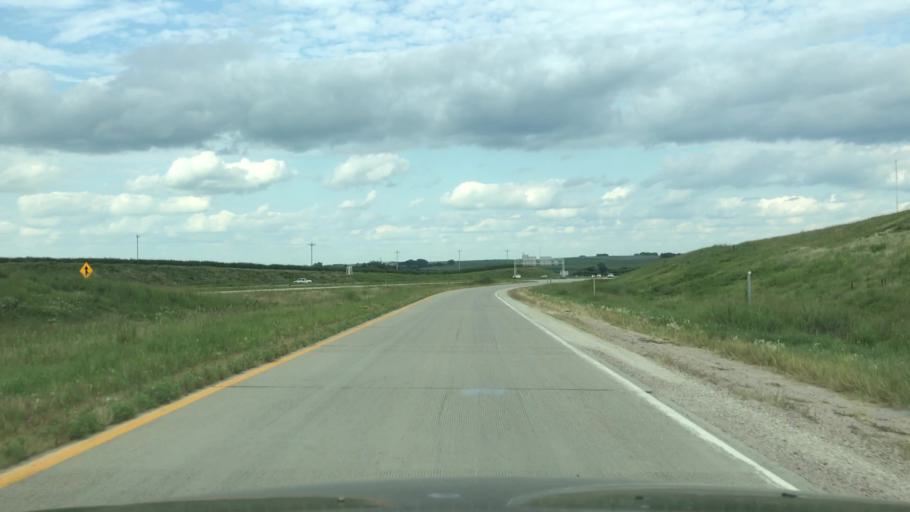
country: US
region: Iowa
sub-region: Plymouth County
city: Le Mars
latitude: 42.8176
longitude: -96.1724
